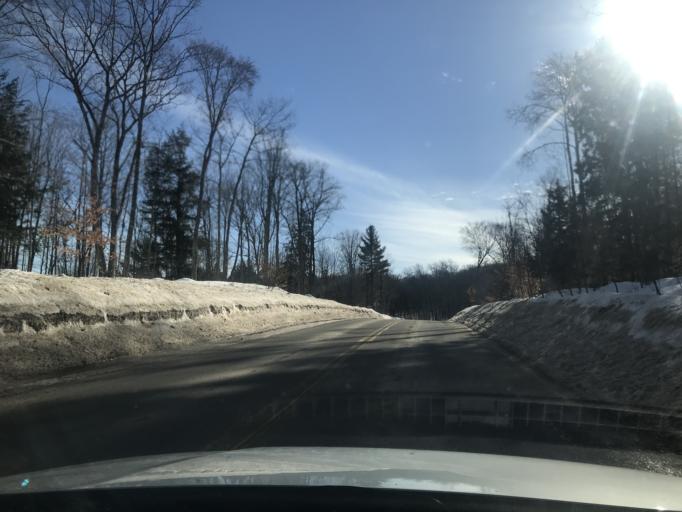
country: US
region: Michigan
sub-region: Dickinson County
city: Kingsford
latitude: 45.4099
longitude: -88.3530
